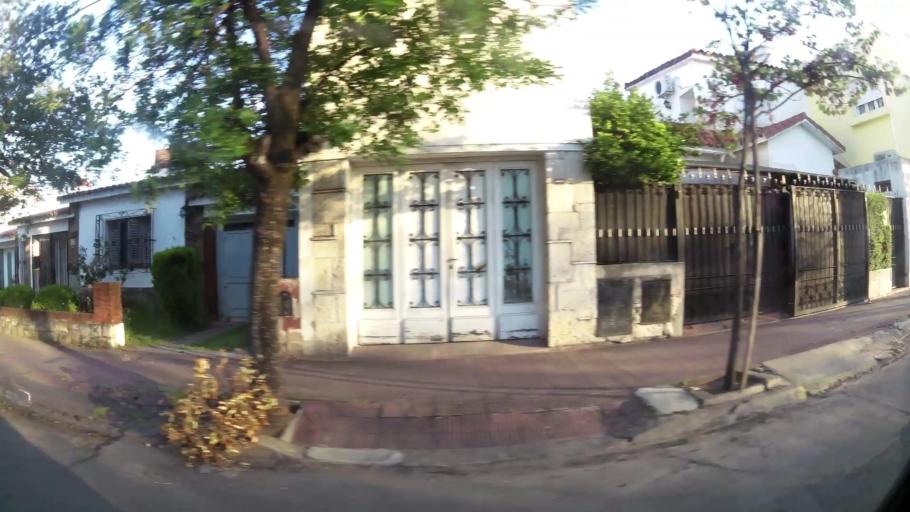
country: AR
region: Cordoba
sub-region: Departamento de Capital
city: Cordoba
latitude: -31.3725
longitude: -64.2343
